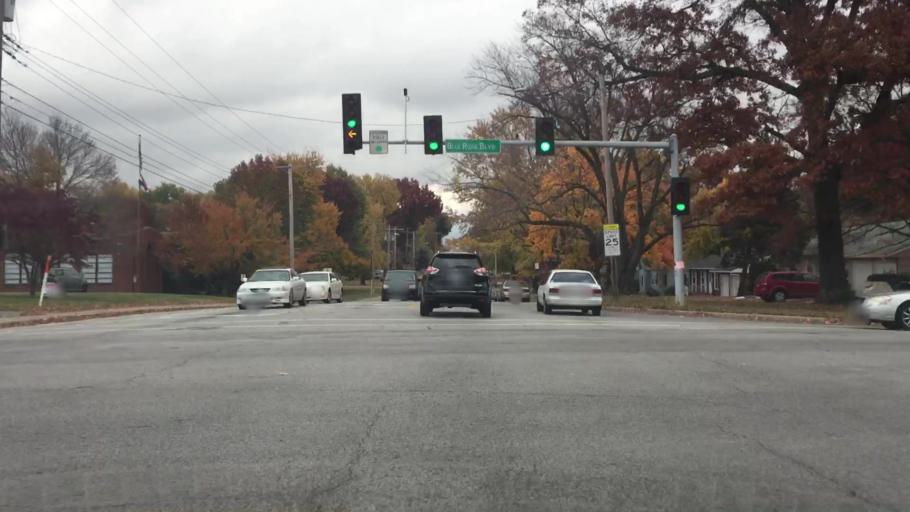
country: US
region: Missouri
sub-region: Jackson County
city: Raytown
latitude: 38.9951
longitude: -94.4824
